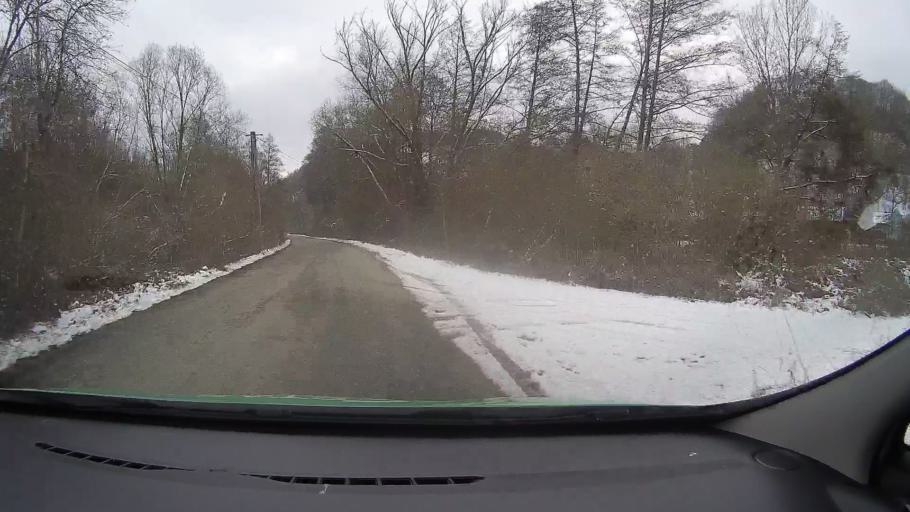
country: RO
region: Hunedoara
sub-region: Comuna Balsa
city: Balsa
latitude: 46.0466
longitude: 23.0687
